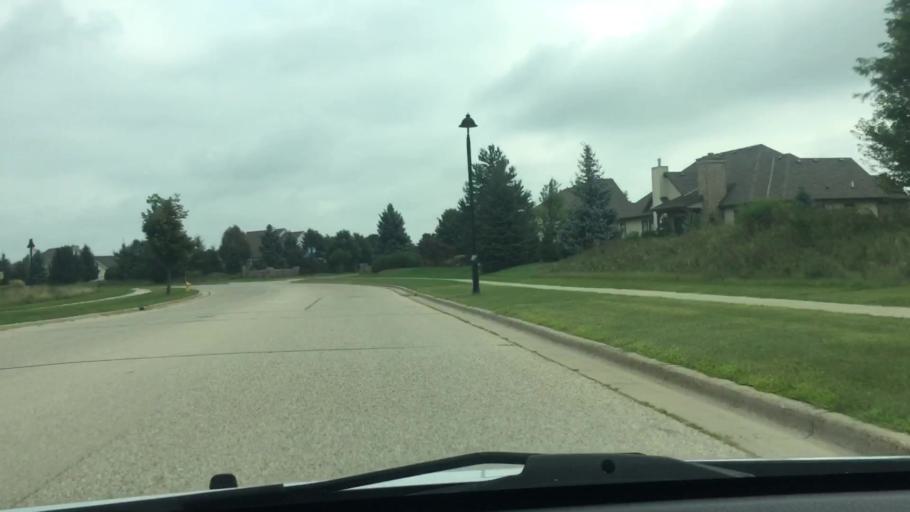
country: US
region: Wisconsin
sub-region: Waukesha County
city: Okauchee Lake
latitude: 43.0735
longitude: -88.4582
